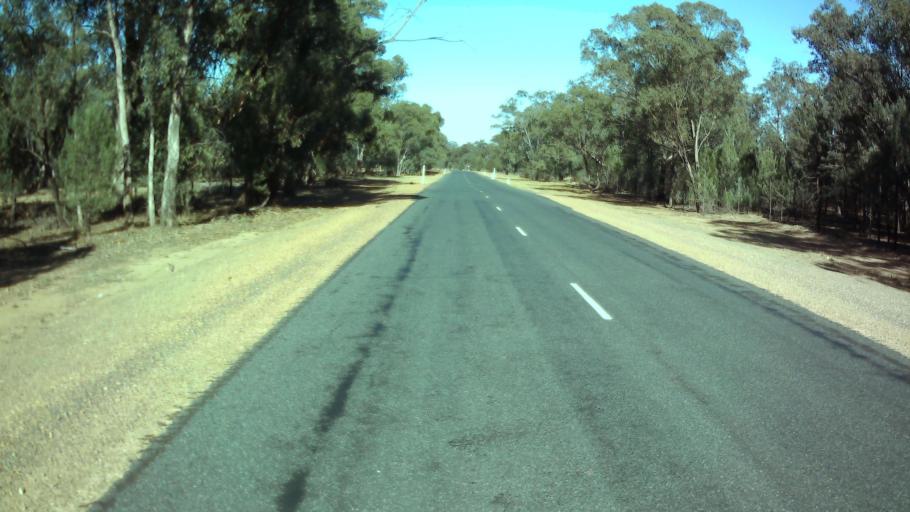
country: AU
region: New South Wales
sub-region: Weddin
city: Grenfell
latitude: -34.0244
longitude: 147.9956
